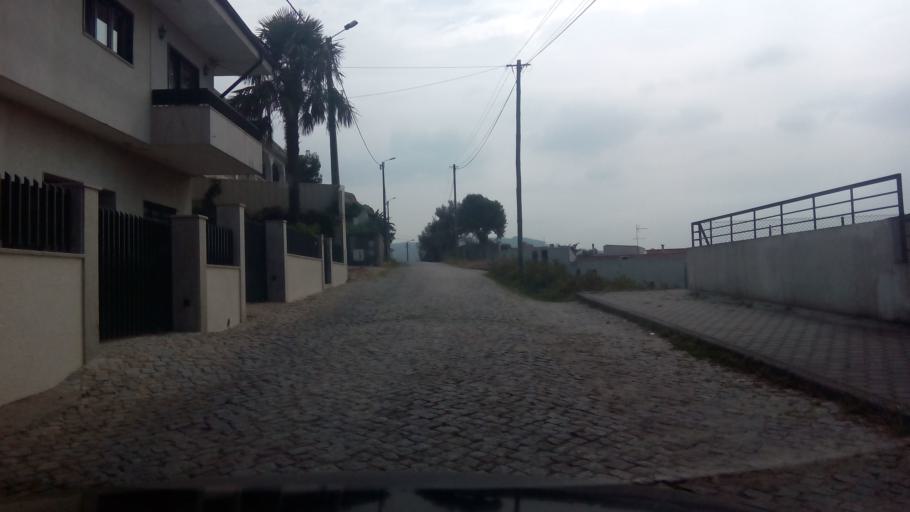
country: PT
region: Porto
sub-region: Paredes
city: Gandra
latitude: 41.1910
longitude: -8.4386
